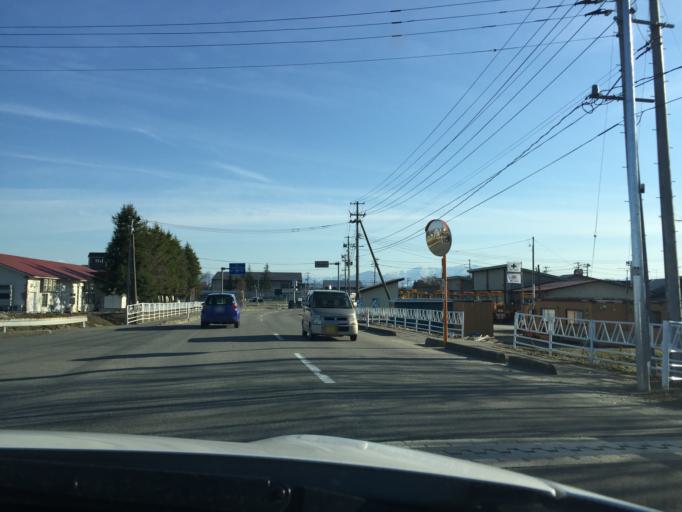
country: JP
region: Yamagata
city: Nagai
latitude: 38.0147
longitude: 140.0553
